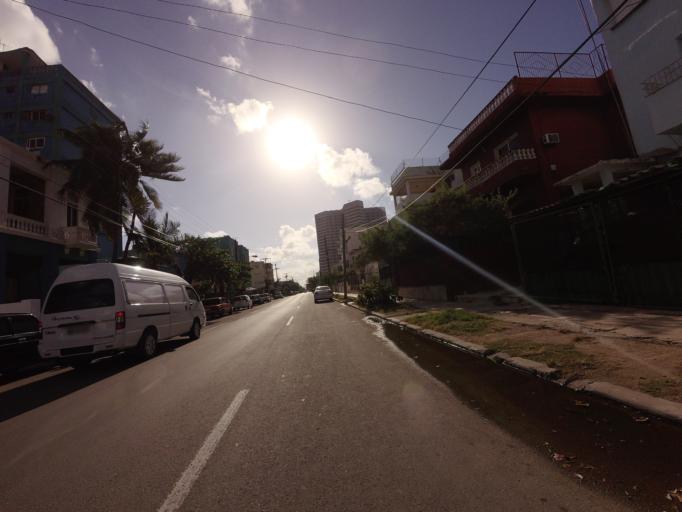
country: CU
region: La Habana
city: Havana
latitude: 23.1410
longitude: -82.4001
